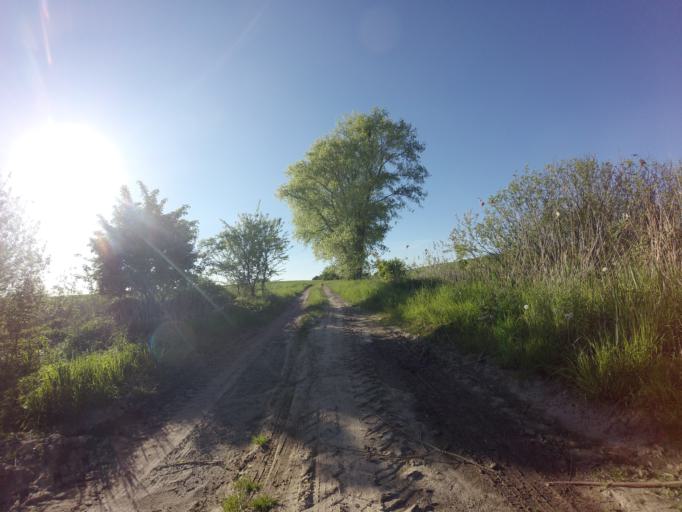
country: PL
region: West Pomeranian Voivodeship
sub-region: Powiat choszczenski
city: Choszczno
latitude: 53.1251
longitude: 15.3618
